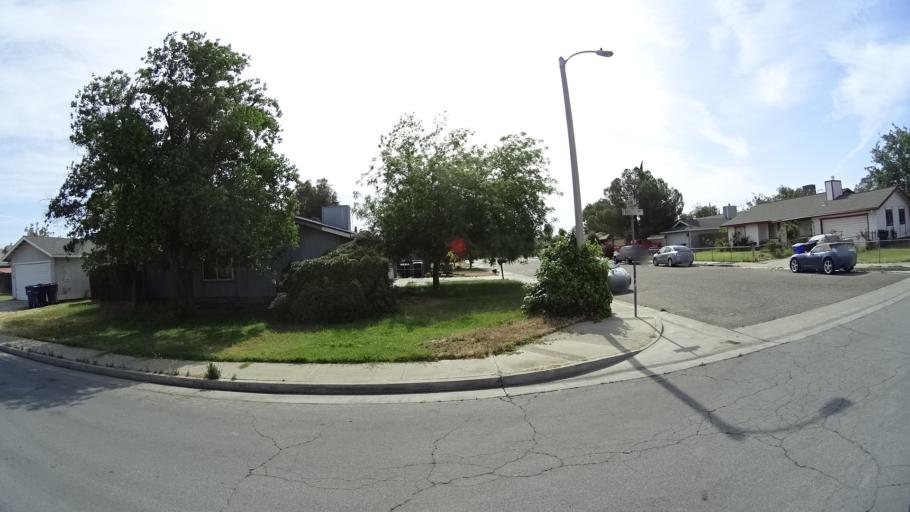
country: US
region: California
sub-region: Kings County
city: Hanford
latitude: 36.3186
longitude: -119.6636
